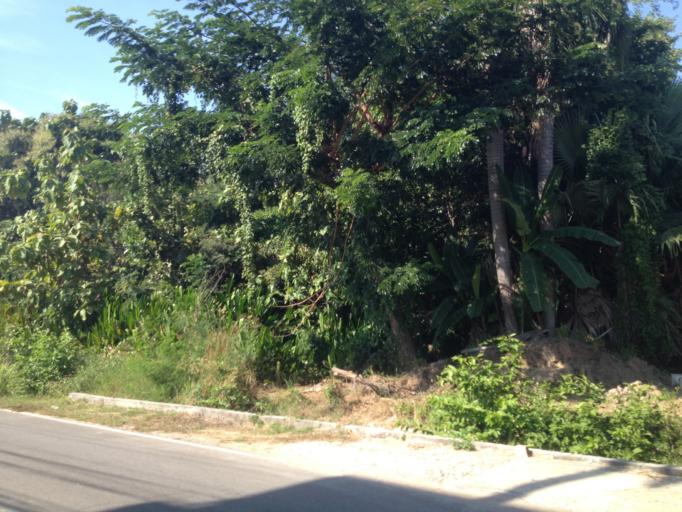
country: TH
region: Chiang Mai
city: Hang Dong
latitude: 18.7235
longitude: 98.9619
